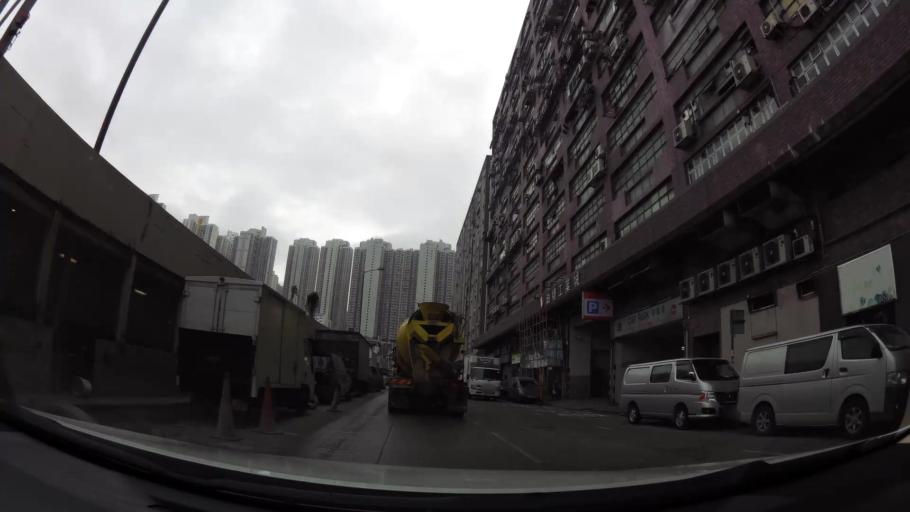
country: HK
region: Kowloon City
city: Kowloon
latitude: 22.2955
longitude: 114.2349
